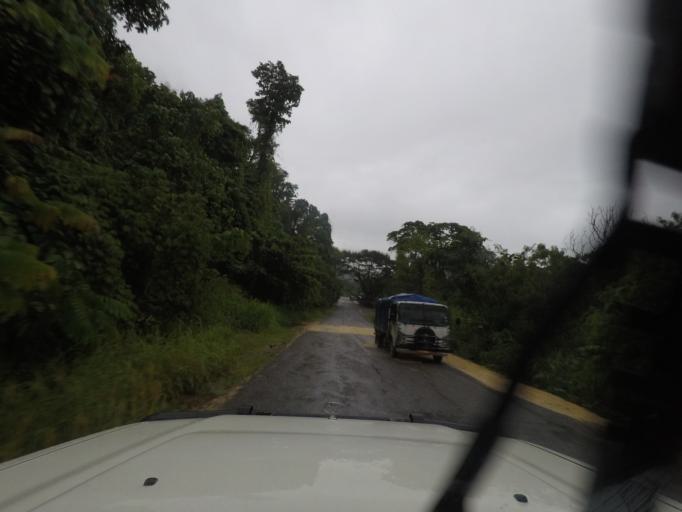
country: PG
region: Madang
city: Madang
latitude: -5.3976
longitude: 145.6301
